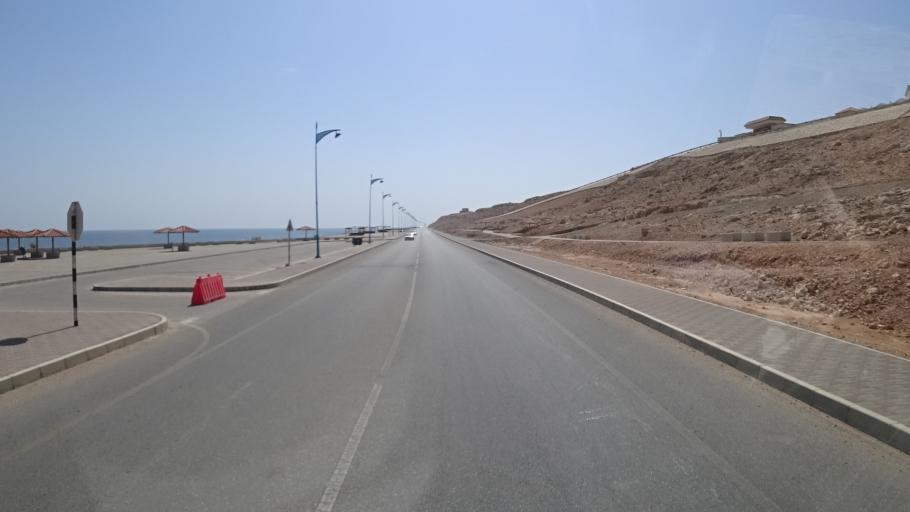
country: OM
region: Ash Sharqiyah
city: Sur
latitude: 22.5665
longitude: 59.5586
